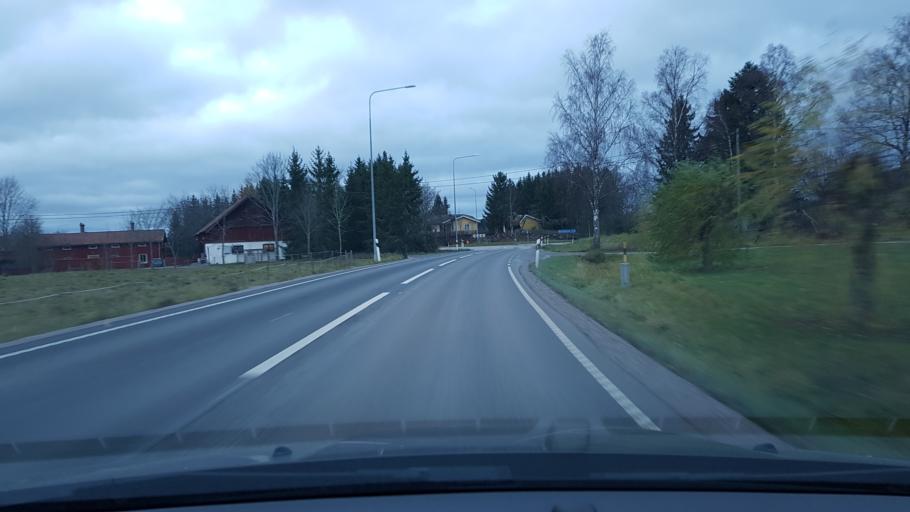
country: SE
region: Uppsala
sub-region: Uppsala Kommun
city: Vattholma
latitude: 59.9518
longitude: 17.8982
